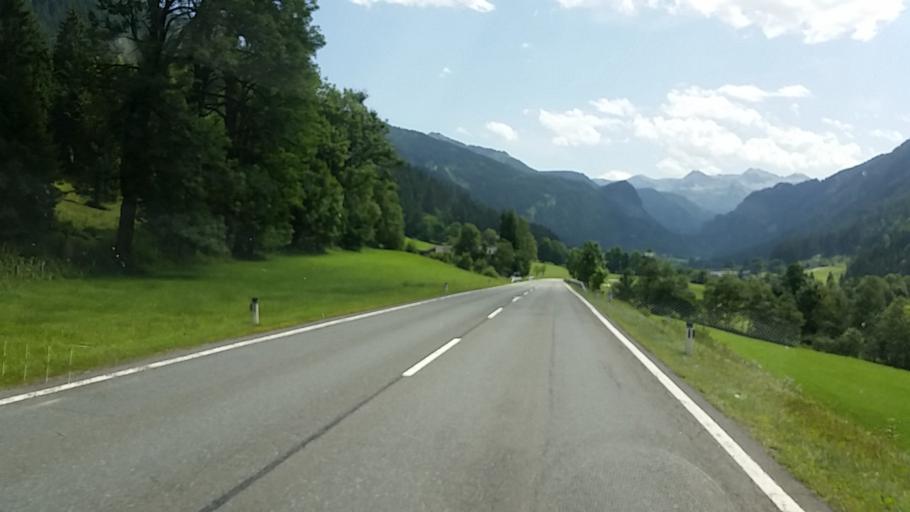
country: AT
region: Salzburg
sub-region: Politischer Bezirk Sankt Johann im Pongau
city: Untertauern
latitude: 47.3330
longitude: 13.5075
